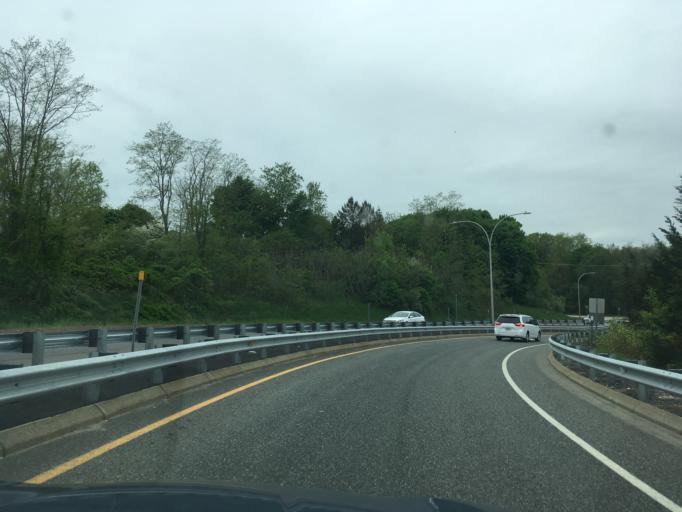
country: US
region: Rhode Island
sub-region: Washington County
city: Exeter
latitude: 41.5793
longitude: -71.5038
